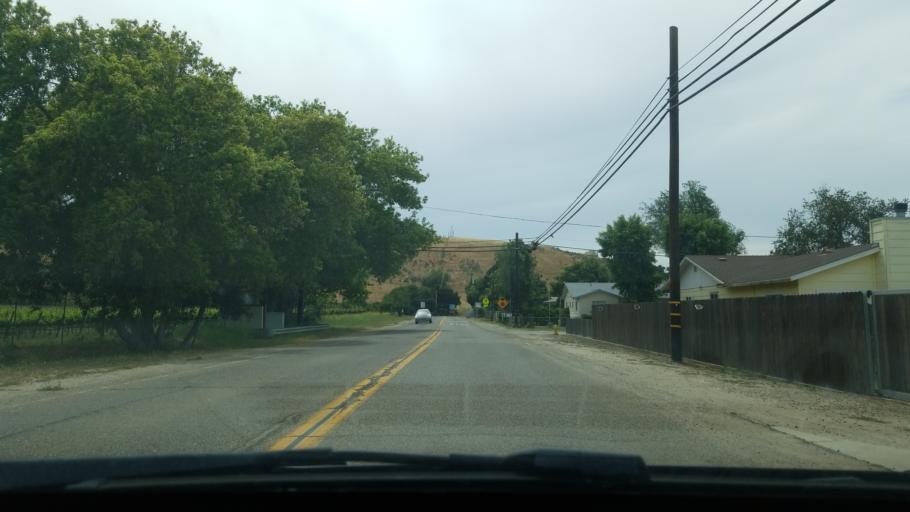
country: US
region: California
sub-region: Santa Barbara County
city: Los Alamos
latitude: 34.8646
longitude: -120.2928
